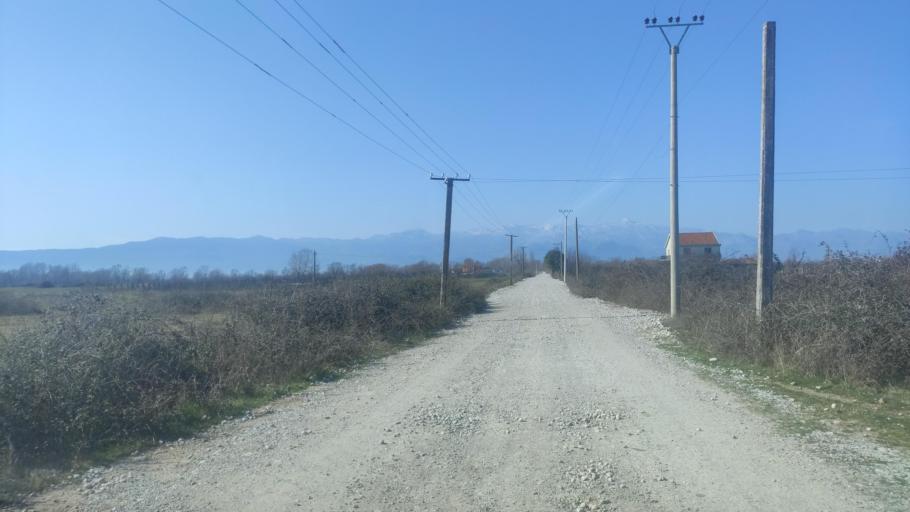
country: AL
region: Shkoder
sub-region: Rrethi i Malesia e Madhe
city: Grude-Fushe
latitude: 42.1597
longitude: 19.4523
